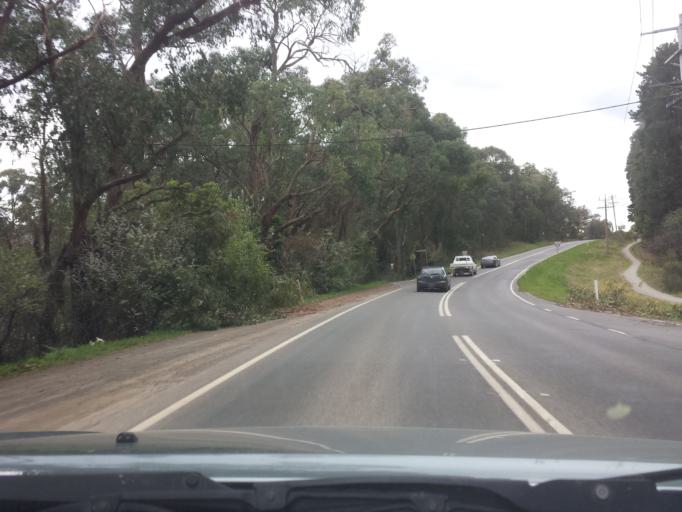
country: AU
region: Victoria
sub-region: Yarra Ranges
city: Mount Evelyn
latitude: -37.7964
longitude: 145.3897
